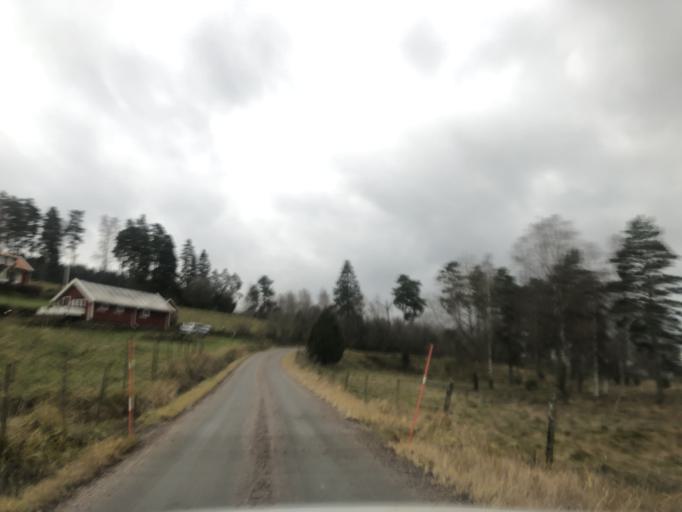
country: SE
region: Vaestra Goetaland
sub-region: Ulricehamns Kommun
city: Ulricehamn
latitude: 57.8886
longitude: 13.4675
